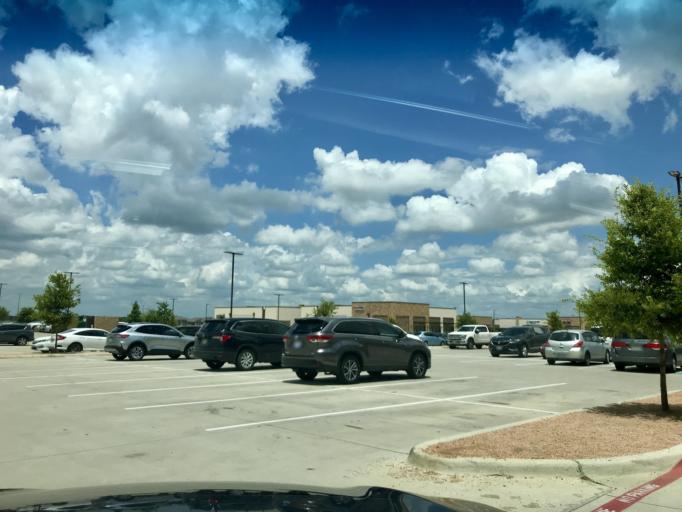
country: US
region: Texas
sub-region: Tarrant County
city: Crowley
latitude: 32.6042
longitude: -97.4099
